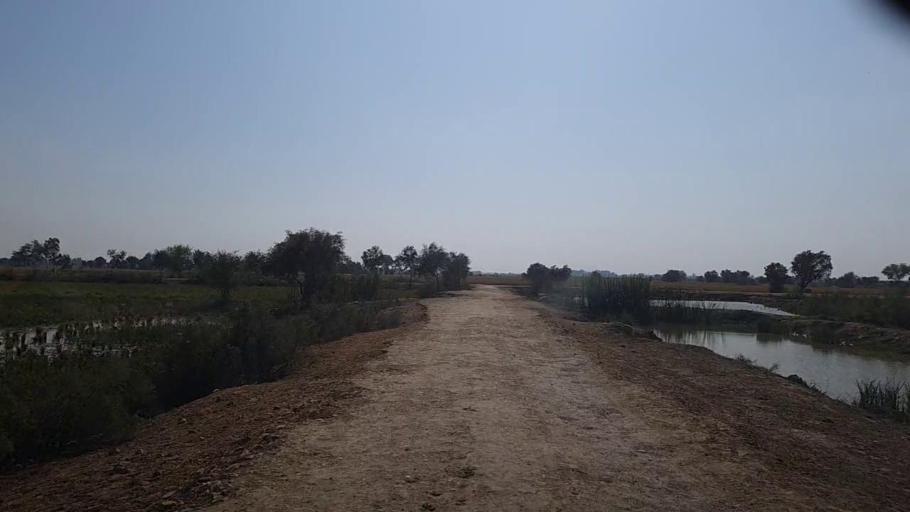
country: PK
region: Sindh
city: Thul
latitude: 28.1679
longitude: 68.7665
